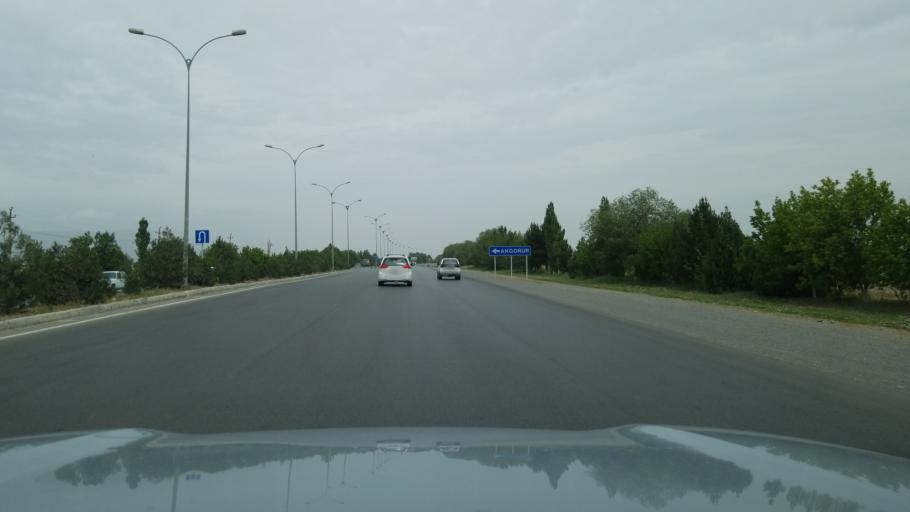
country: TM
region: Ahal
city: Abadan
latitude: 38.1042
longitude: 58.0718
